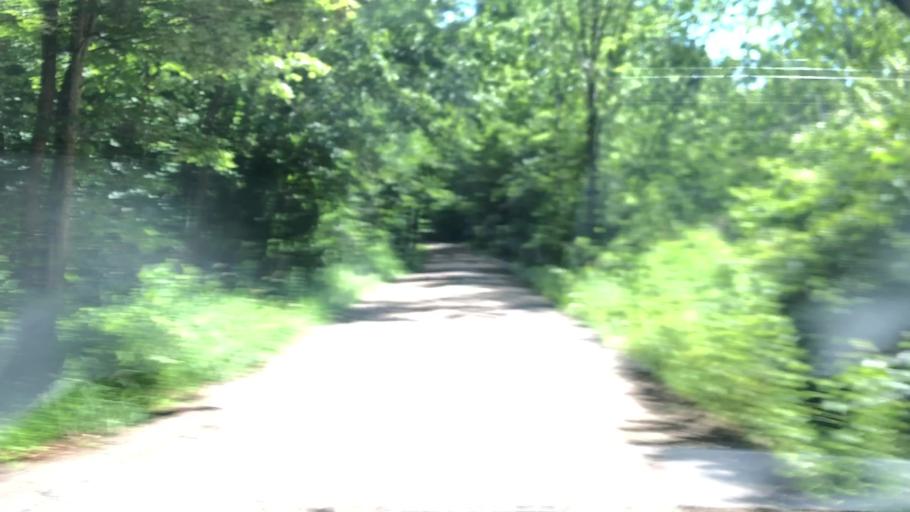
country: US
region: New Hampshire
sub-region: Hillsborough County
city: Milford
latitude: 42.8570
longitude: -71.5858
